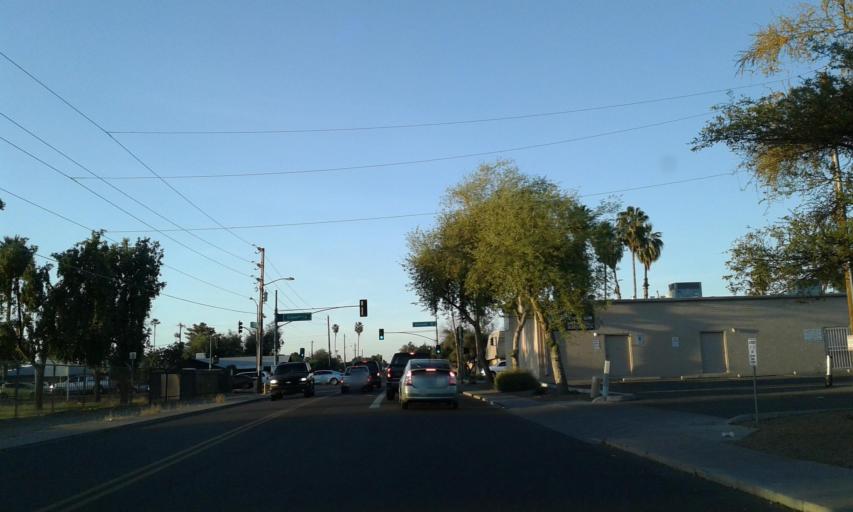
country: US
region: Arizona
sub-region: Maricopa County
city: Glendale
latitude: 33.5379
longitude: -112.1039
